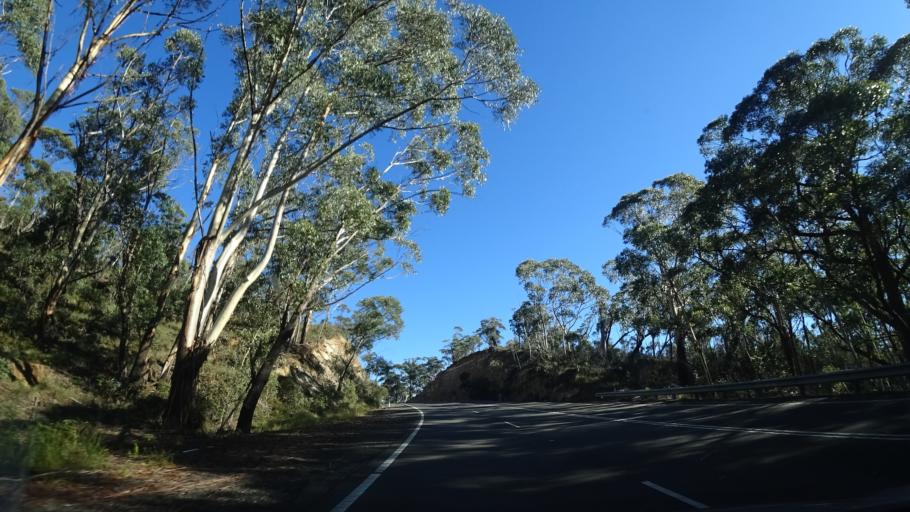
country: AU
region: New South Wales
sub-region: Blue Mountains Municipality
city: Blackheath
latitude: -33.5201
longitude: 150.3050
